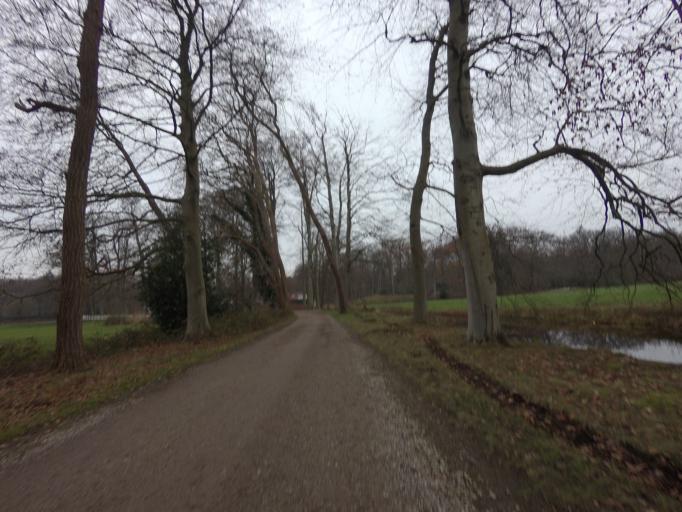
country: NL
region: North Holland
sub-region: Gemeente Wijdemeren
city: Kortenhoef
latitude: 52.2423
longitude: 5.1388
